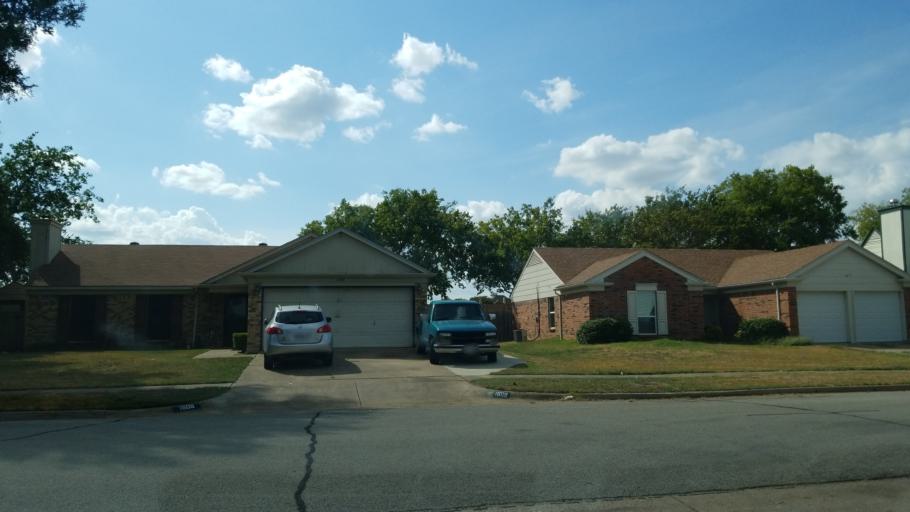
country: US
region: Texas
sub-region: Tarrant County
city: Euless
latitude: 32.8600
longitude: -97.0776
